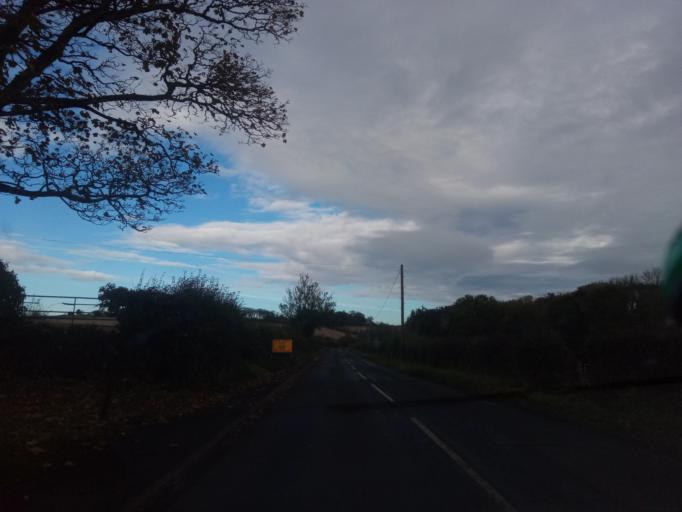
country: GB
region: Scotland
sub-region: The Scottish Borders
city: Eyemouth
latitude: 55.8622
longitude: -2.1003
